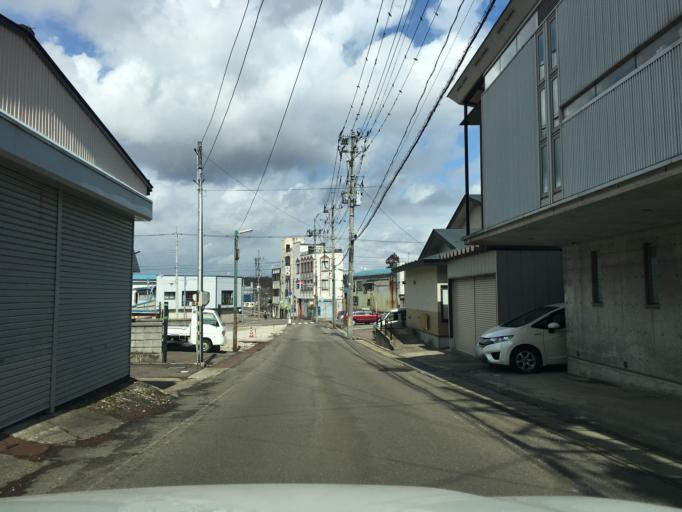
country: JP
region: Akita
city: Takanosu
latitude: 40.1191
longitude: 140.3678
